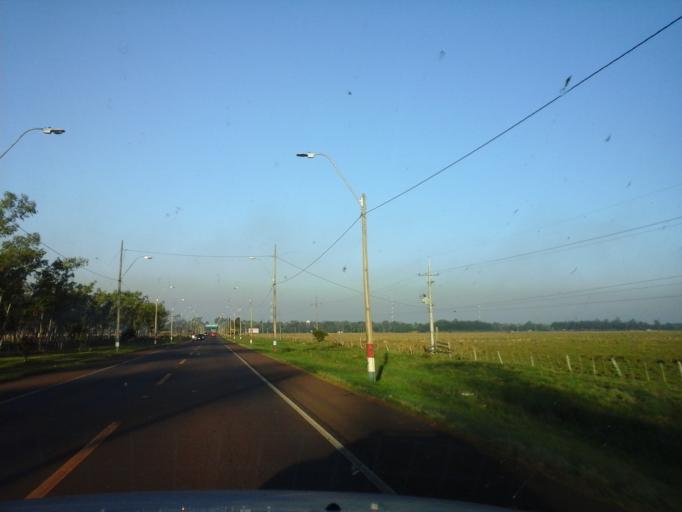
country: PY
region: Itapua
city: General Delgado
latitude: -27.0864
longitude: -56.5367
